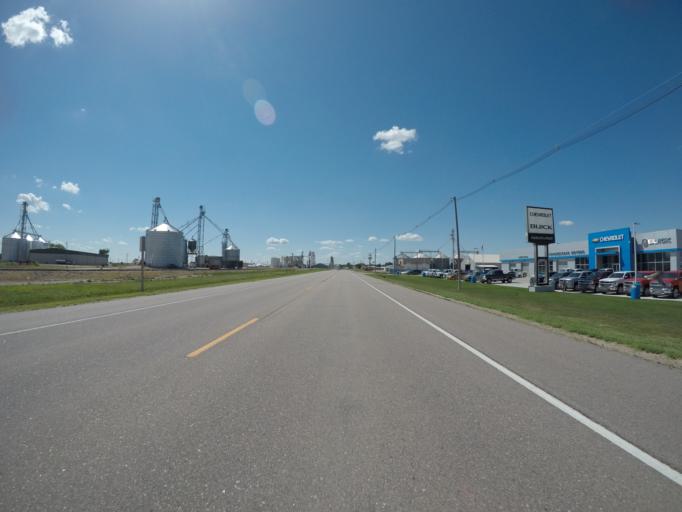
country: US
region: Nebraska
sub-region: Chase County
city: Imperial
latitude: 40.5092
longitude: -101.6336
